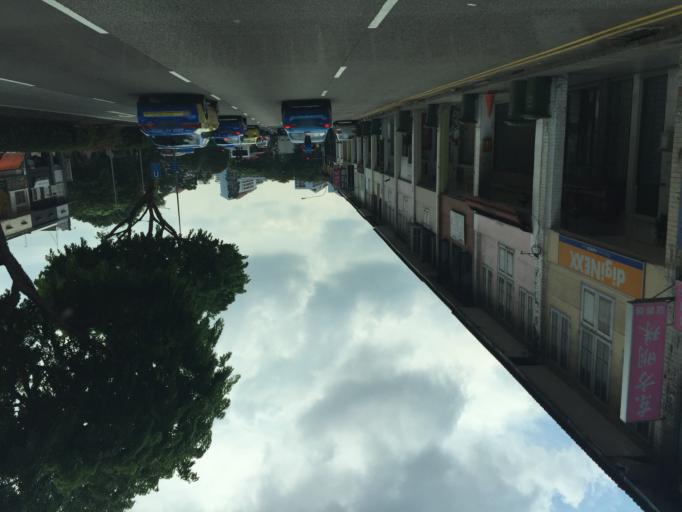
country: SG
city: Singapore
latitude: 1.3150
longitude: 103.8595
